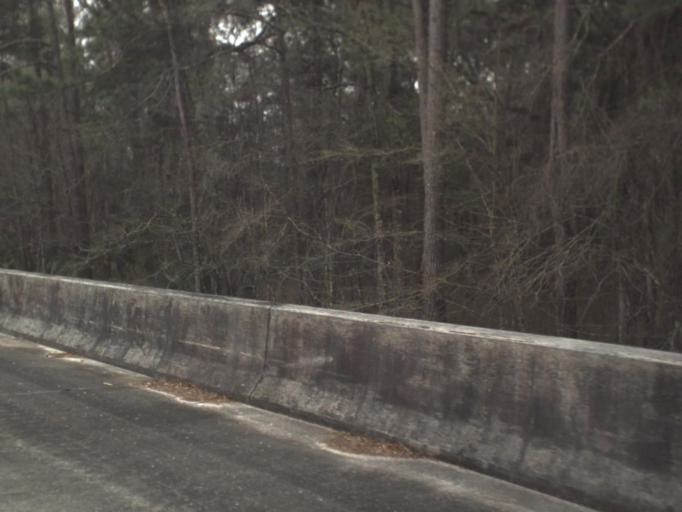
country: US
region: Florida
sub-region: Leon County
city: Woodville
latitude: 30.4079
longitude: -84.0642
